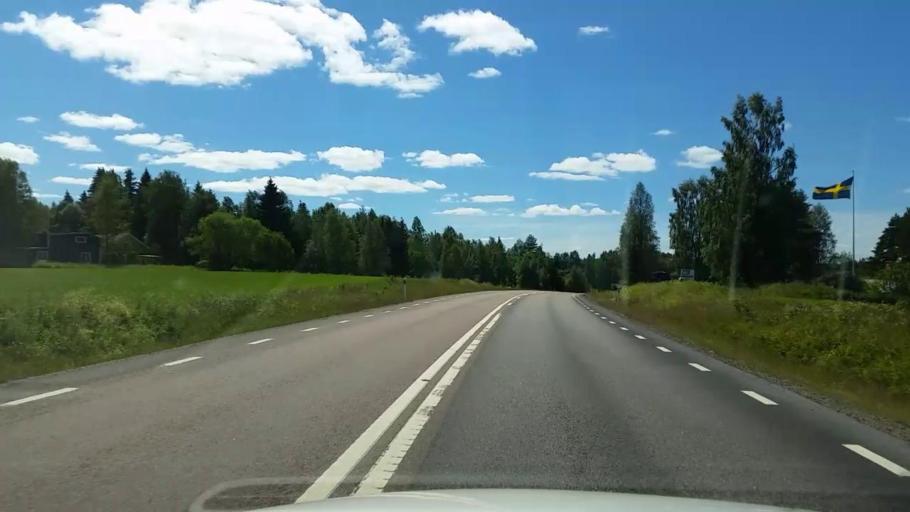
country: SE
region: Gaevleborg
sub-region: Ljusdals Kommun
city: Farila
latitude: 61.8111
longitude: 15.9561
